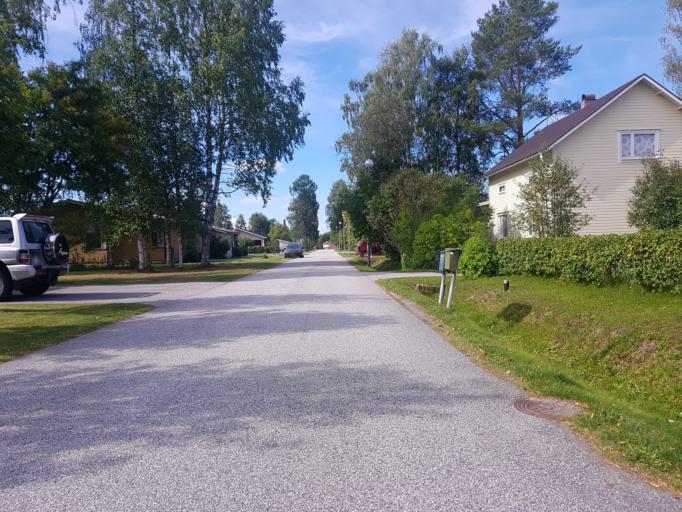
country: FI
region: Kainuu
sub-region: Kehys-Kainuu
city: Kuhmo
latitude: 64.1242
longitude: 29.5230
